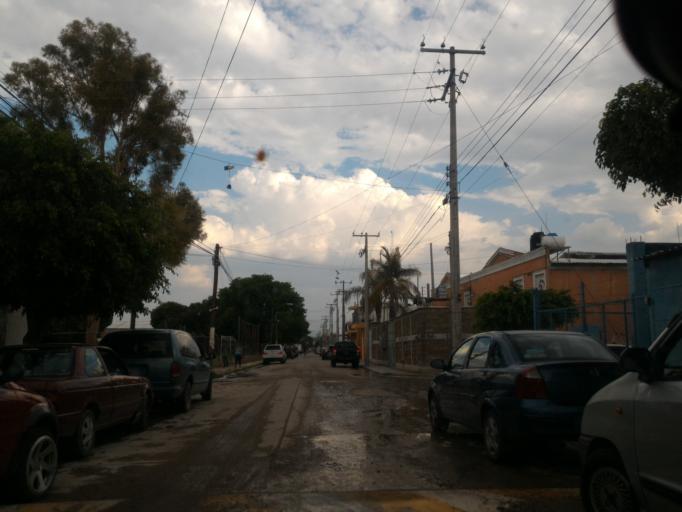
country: MX
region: Guanajuato
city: San Francisco del Rincon
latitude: 21.0348
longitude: -101.8581
